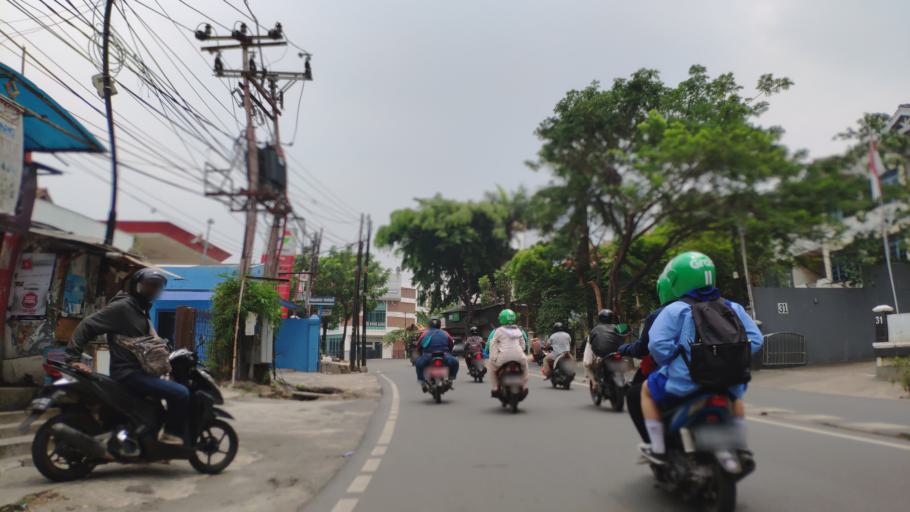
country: ID
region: Banten
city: South Tangerang
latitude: -6.2604
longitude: 106.7766
